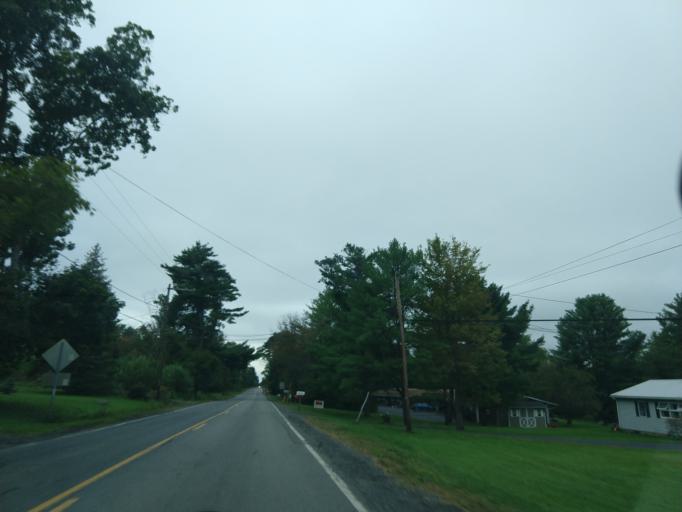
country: US
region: New York
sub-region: Tompkins County
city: East Ithaca
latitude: 42.4087
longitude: -76.4702
